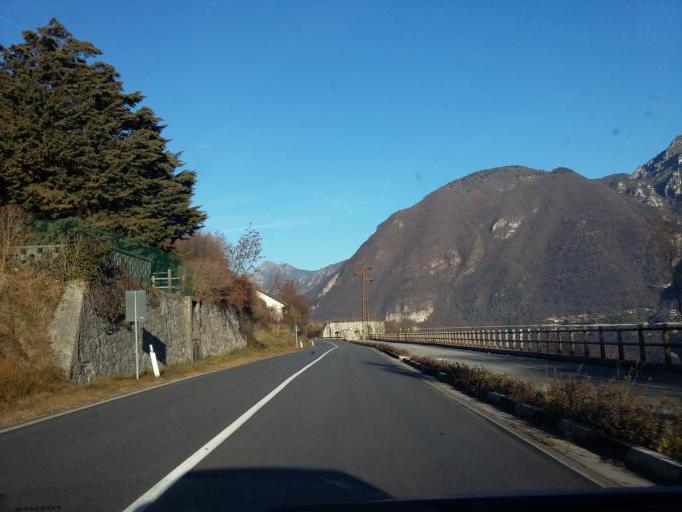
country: IT
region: Lombardy
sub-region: Provincia di Brescia
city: Anfo
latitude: 45.7721
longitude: 10.5002
